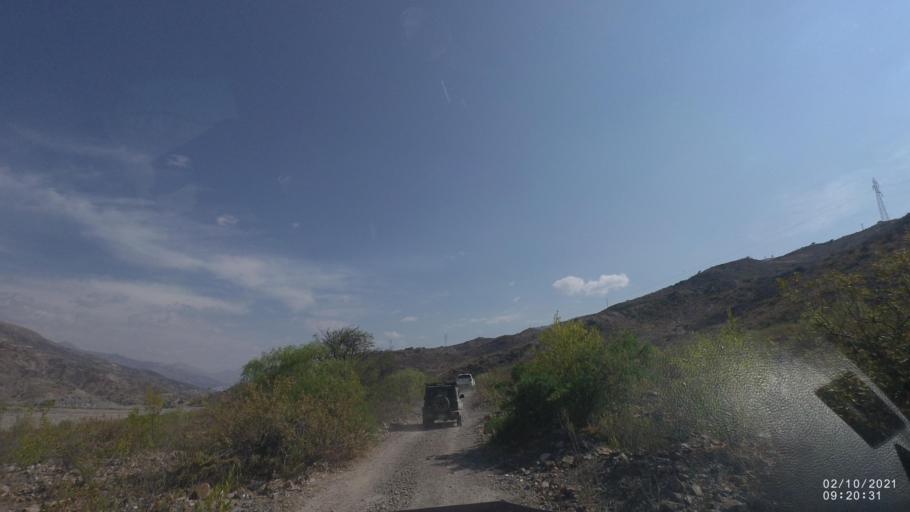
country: BO
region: Cochabamba
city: Irpa Irpa
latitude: -17.8736
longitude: -66.3073
